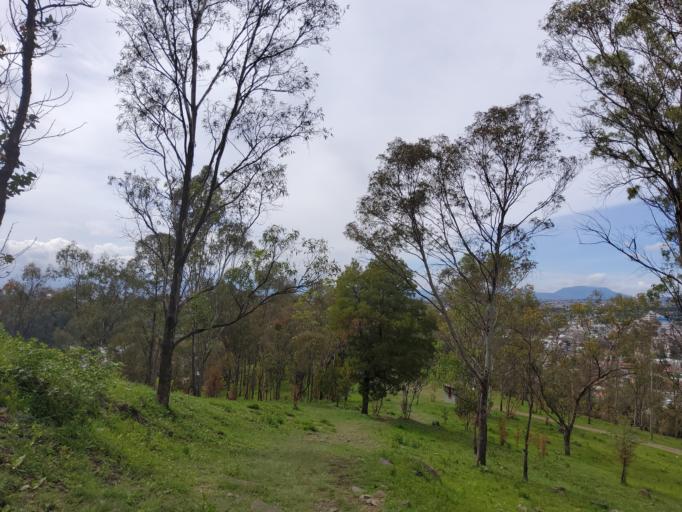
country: MX
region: Mexico
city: Toluca
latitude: 19.3018
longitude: -99.6576
